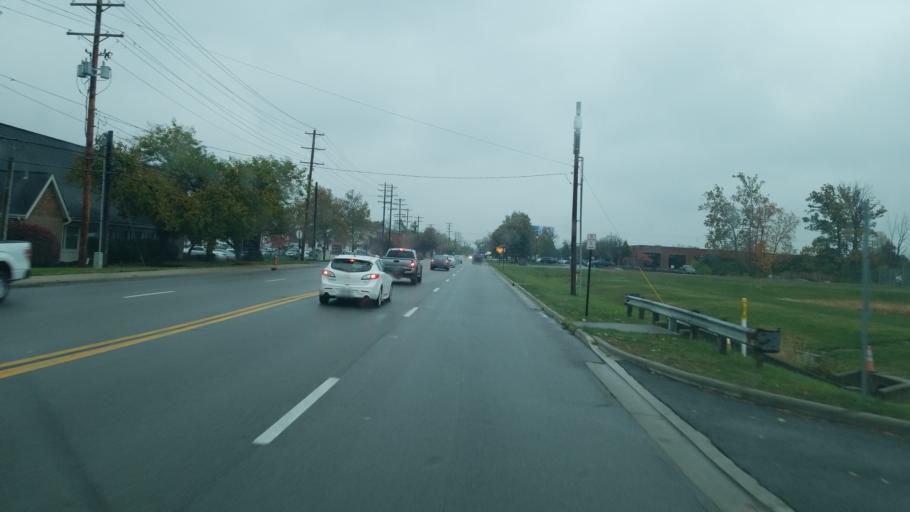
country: US
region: Ohio
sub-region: Franklin County
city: Grandview Heights
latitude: 40.0007
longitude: -83.0346
